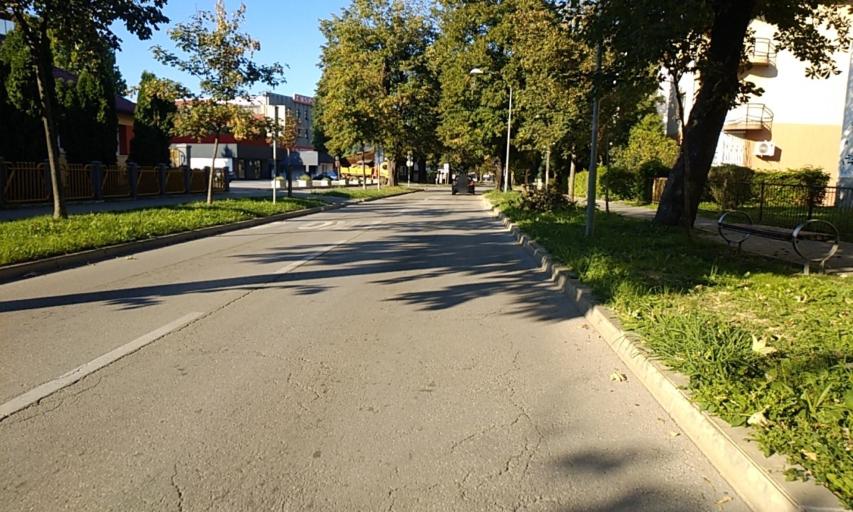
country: BA
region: Republika Srpska
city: Banja Luka
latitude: 44.7740
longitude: 17.1868
